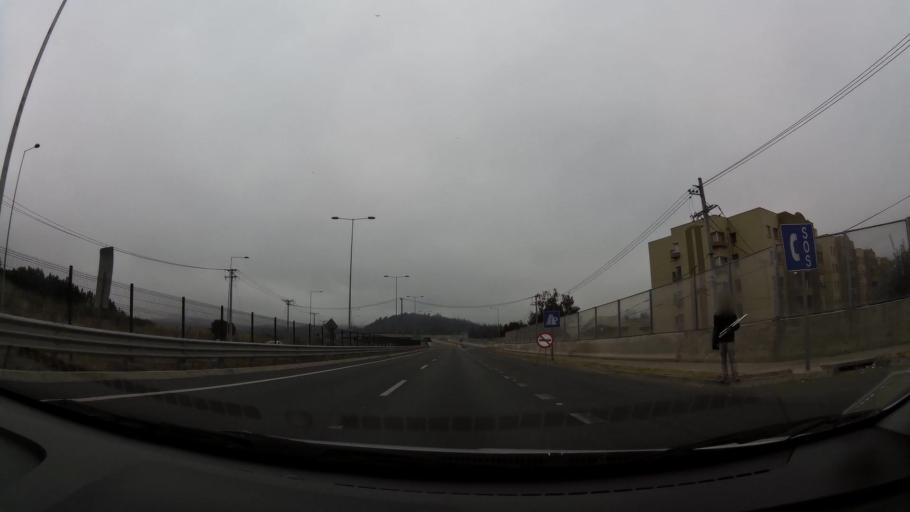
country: CL
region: Biobio
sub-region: Provincia de Concepcion
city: Concepcion
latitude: -36.8159
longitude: -73.0192
